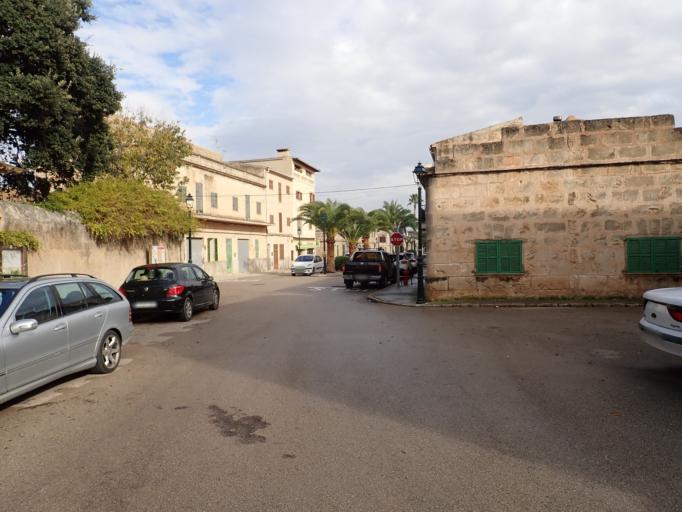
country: ES
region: Balearic Islands
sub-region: Illes Balears
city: Petra
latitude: 39.6154
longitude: 3.1117
